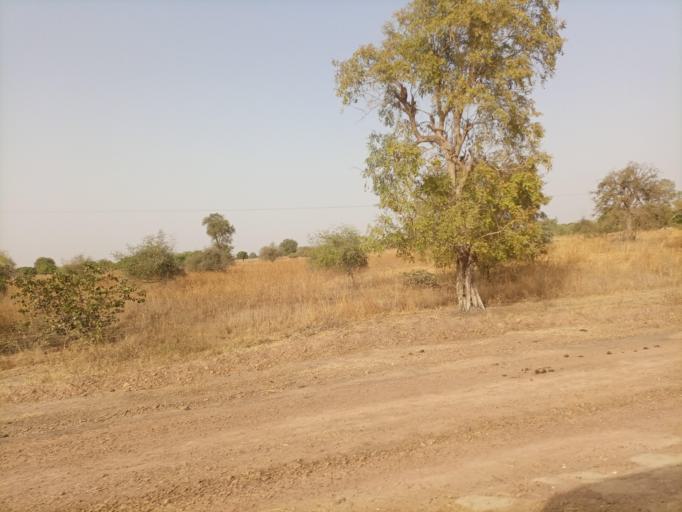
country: SN
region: Fatick
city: Passi
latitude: 14.0236
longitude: -16.3006
